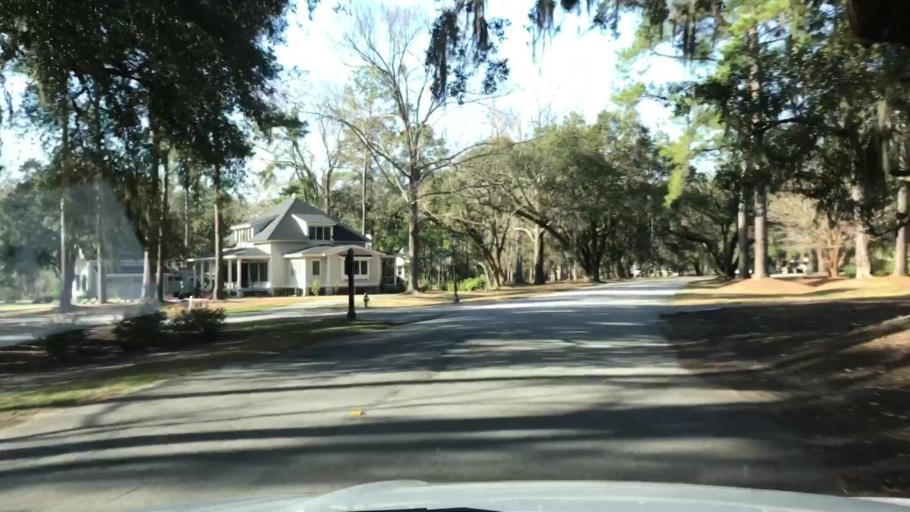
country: US
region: South Carolina
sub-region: Beaufort County
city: Bluffton
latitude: 32.3363
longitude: -80.9097
